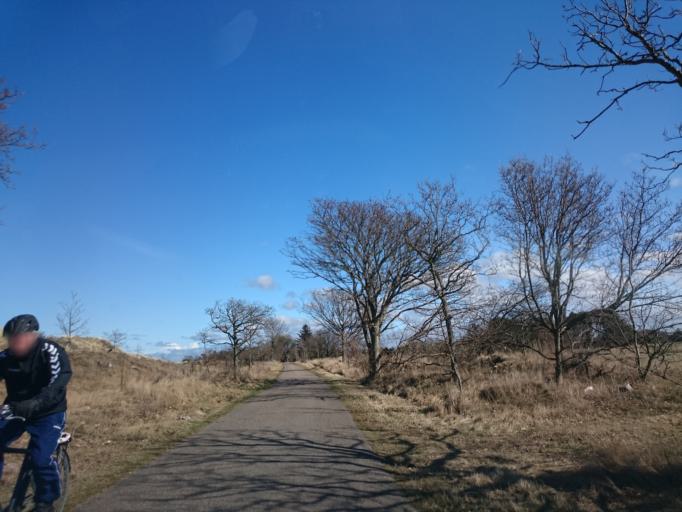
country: DK
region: North Denmark
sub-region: Frederikshavn Kommune
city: Skagen
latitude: 57.6678
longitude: 10.4823
